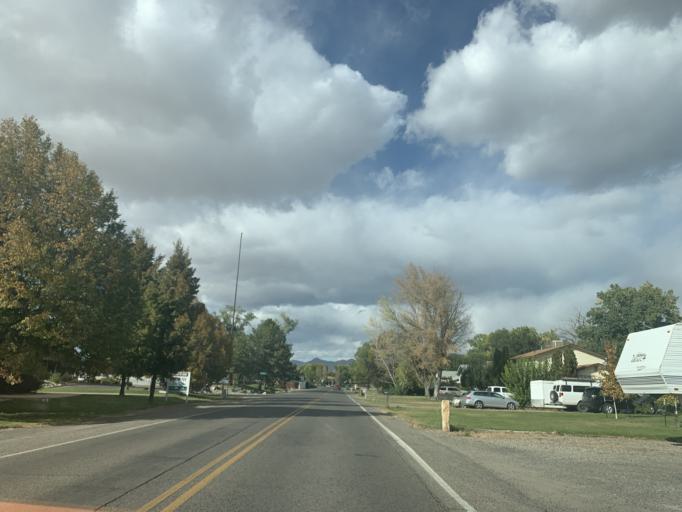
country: US
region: Colorado
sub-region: Mesa County
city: Fruitvale
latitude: 39.0825
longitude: -108.4785
